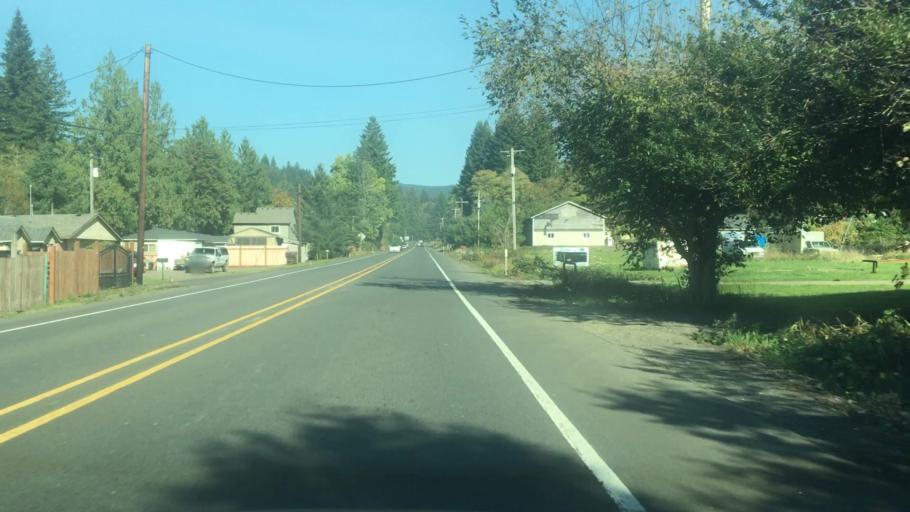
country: US
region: Oregon
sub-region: Lincoln County
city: Rose Lodge
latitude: 45.0139
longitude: -123.8739
